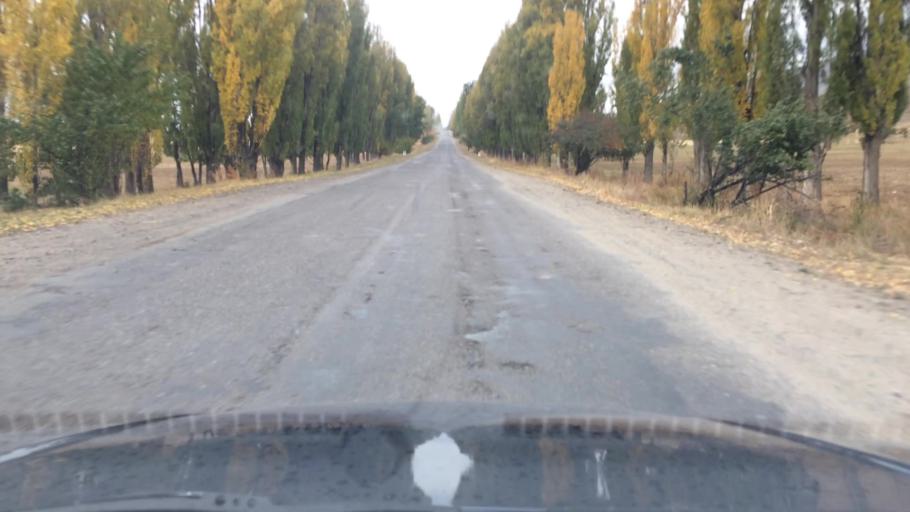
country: KG
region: Ysyk-Koel
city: Pokrovka
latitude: 42.7362
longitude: 77.9609
